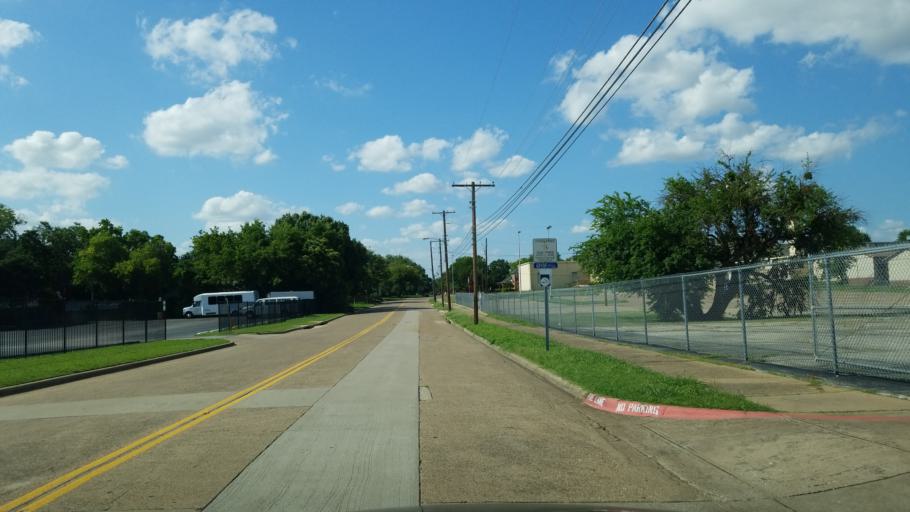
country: US
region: Texas
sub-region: Dallas County
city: University Park
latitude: 32.8815
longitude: -96.8489
